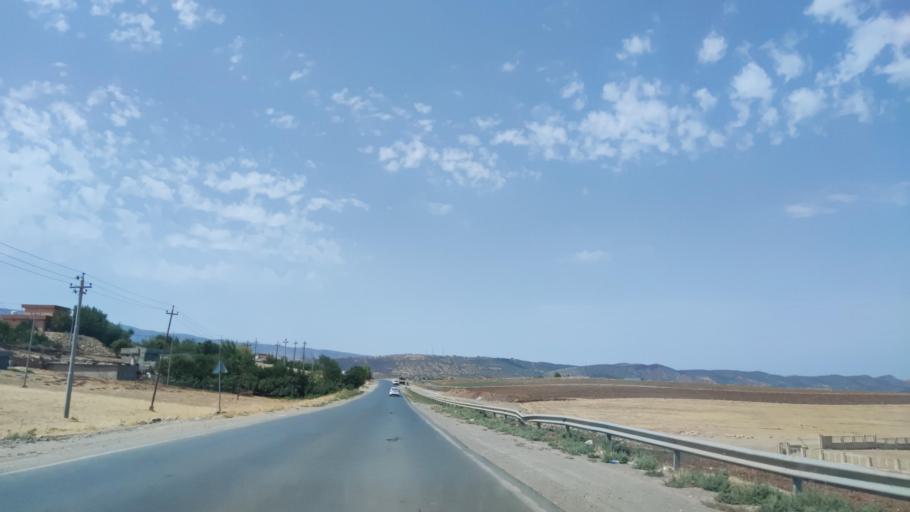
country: IQ
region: Arbil
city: Shaqlawah
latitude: 36.4652
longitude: 44.3948
